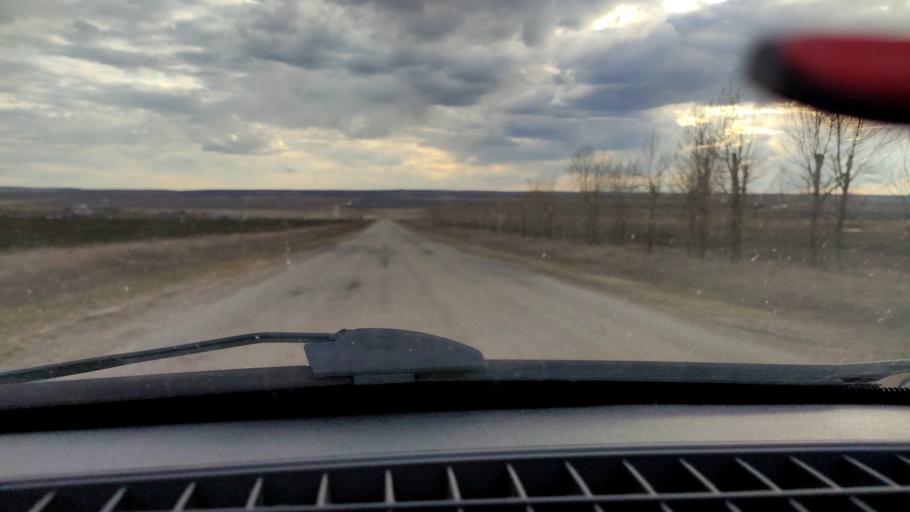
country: RU
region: Bashkortostan
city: Karmaskaly
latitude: 54.2974
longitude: 55.9193
